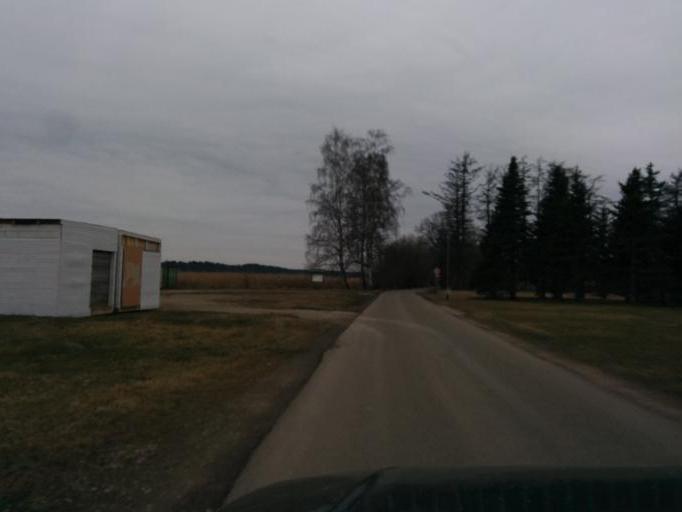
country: LV
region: Babite
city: Pinki
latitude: 56.9710
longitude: 23.8512
